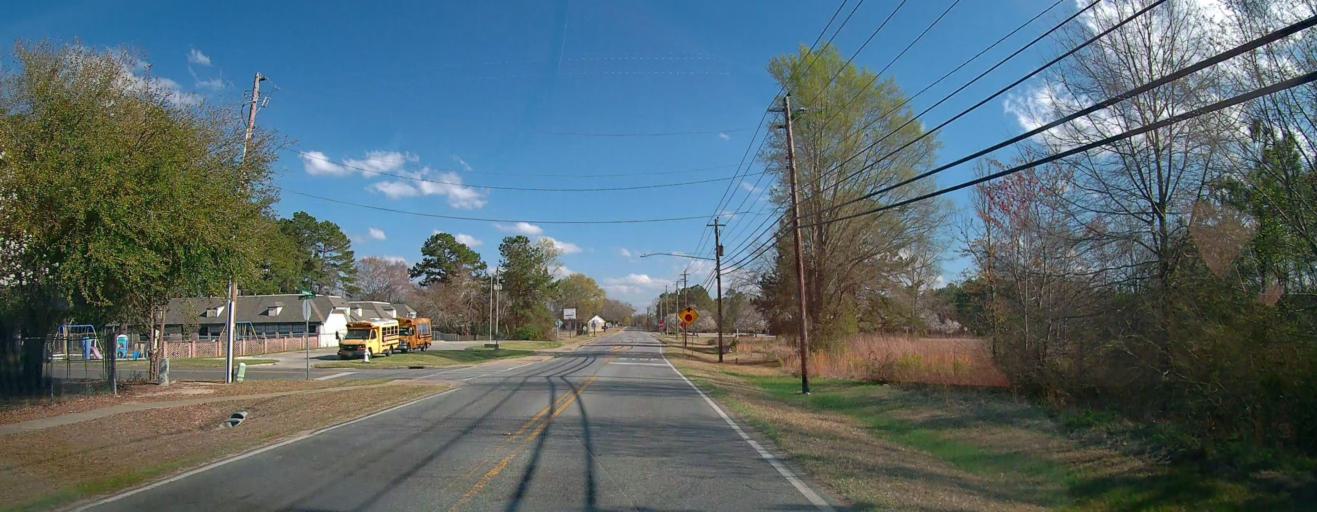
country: US
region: Georgia
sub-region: Laurens County
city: Dublin
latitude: 32.5459
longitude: -82.9222
